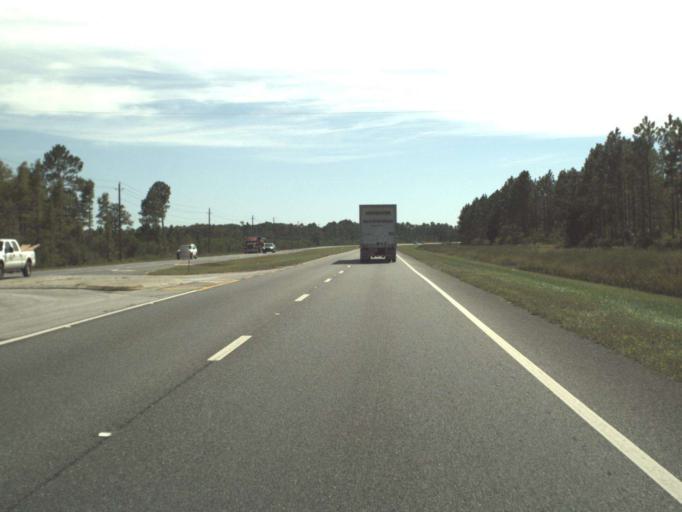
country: US
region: Florida
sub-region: Bay County
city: Lynn Haven
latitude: 30.3452
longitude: -85.6625
